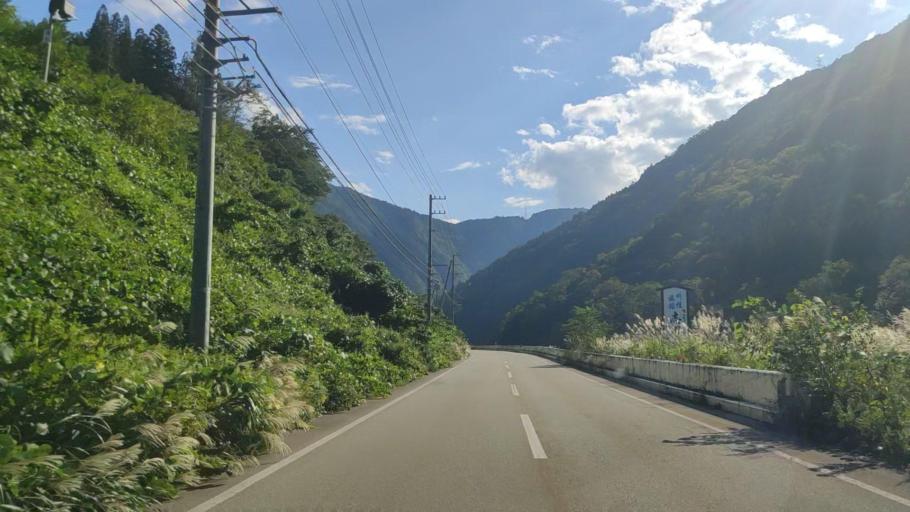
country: JP
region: Gifu
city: Takayama
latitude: 36.3242
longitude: 137.1361
